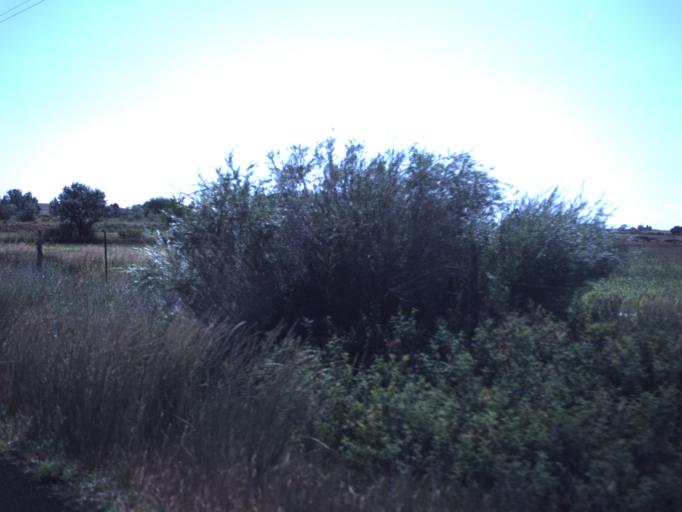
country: US
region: Utah
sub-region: Uintah County
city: Maeser
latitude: 40.4038
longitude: -109.7870
